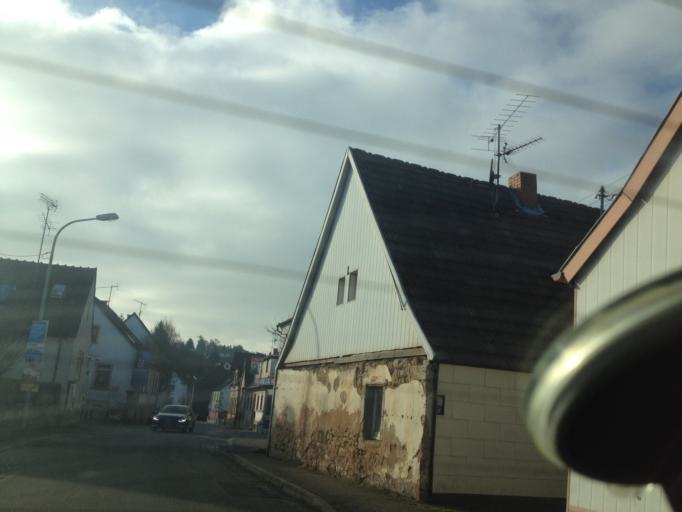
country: DE
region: Rheinland-Pfalz
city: Borsborn
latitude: 49.4538
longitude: 7.3855
